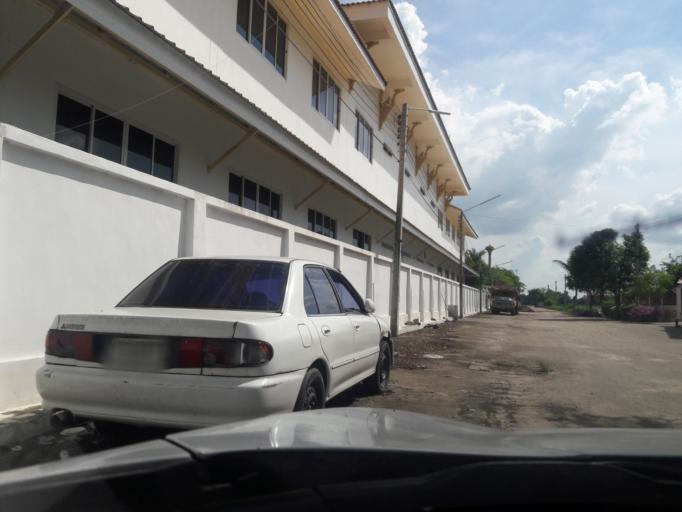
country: TH
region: Lop Buri
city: Ban Mi
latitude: 14.9709
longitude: 100.5235
